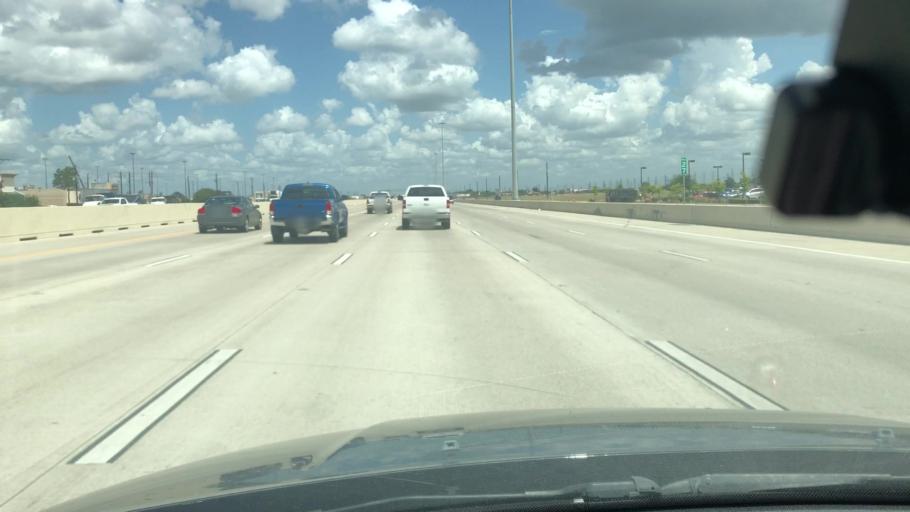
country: US
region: Texas
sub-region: Harris County
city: Webster
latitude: 29.5443
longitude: -95.1449
